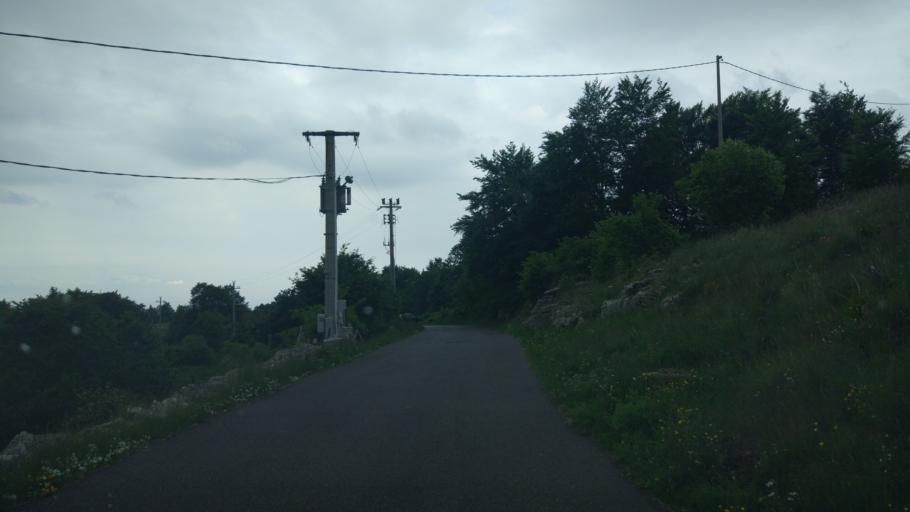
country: IT
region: Veneto
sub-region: Provincia di Verona
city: Erbezzo
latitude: 45.6619
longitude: 11.0010
